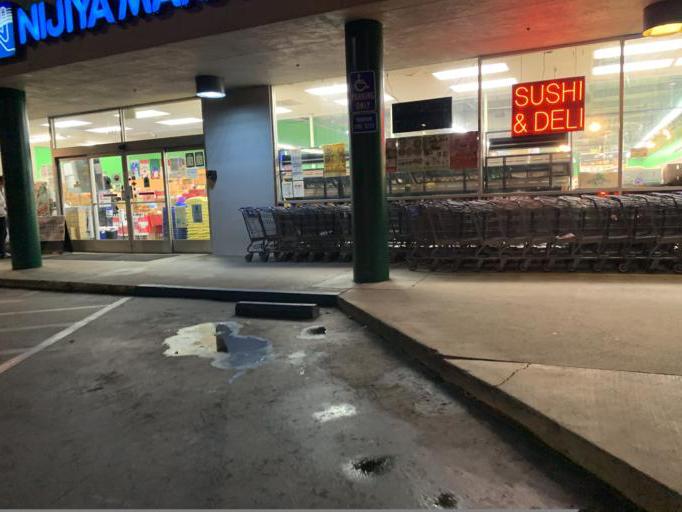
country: US
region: California
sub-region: Santa Clara County
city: Mountain View
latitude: 37.3788
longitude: -122.0715
